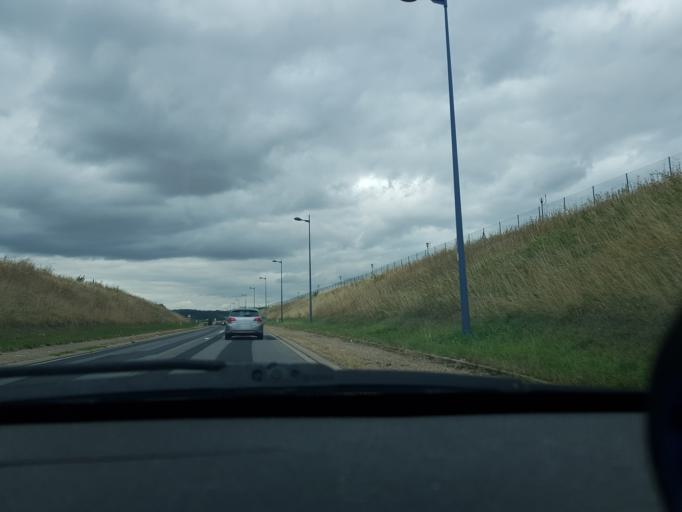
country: FR
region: Lorraine
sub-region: Departement de Meurthe-et-Moselle
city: Saulxures-les-Nancy
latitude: 48.6952
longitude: 6.2417
